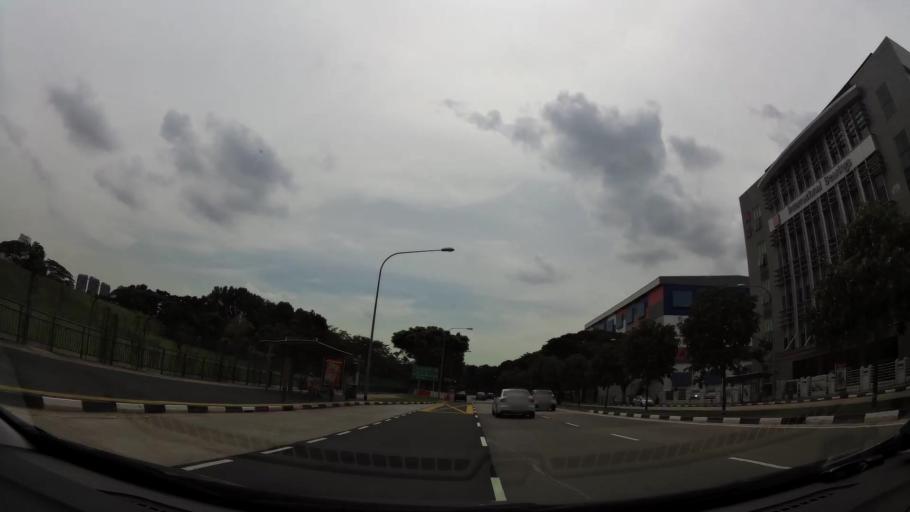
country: SG
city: Singapore
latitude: 1.3301
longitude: 103.7585
